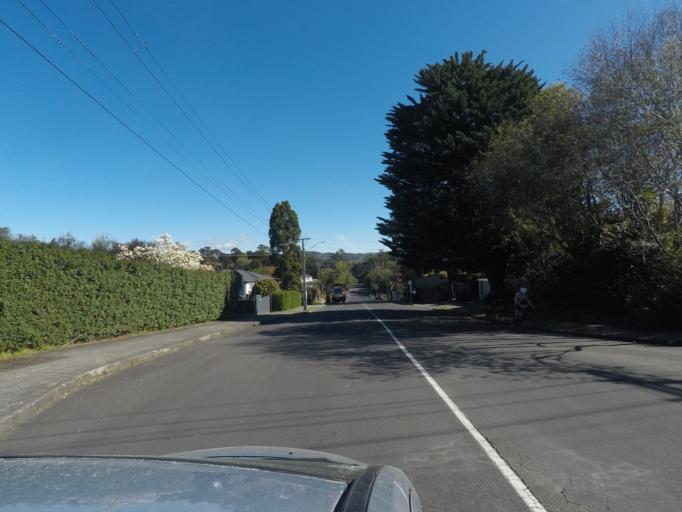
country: NZ
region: Auckland
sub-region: Auckland
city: Waitakere
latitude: -36.9288
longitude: 174.6953
